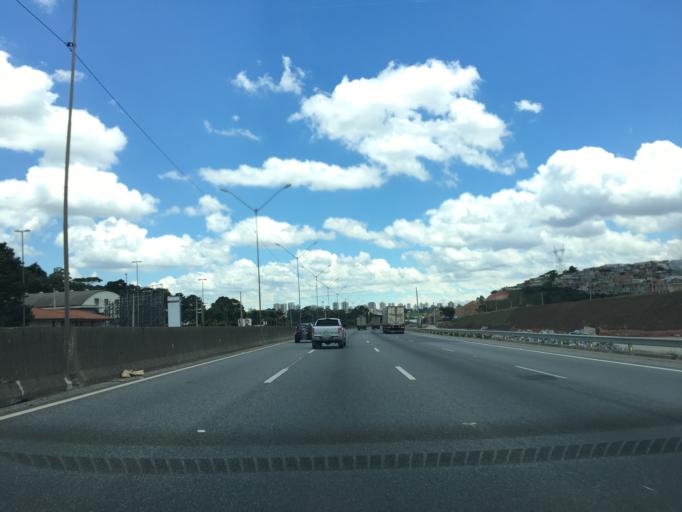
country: BR
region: Sao Paulo
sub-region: Guarulhos
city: Guarulhos
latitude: -23.4258
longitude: -46.5733
